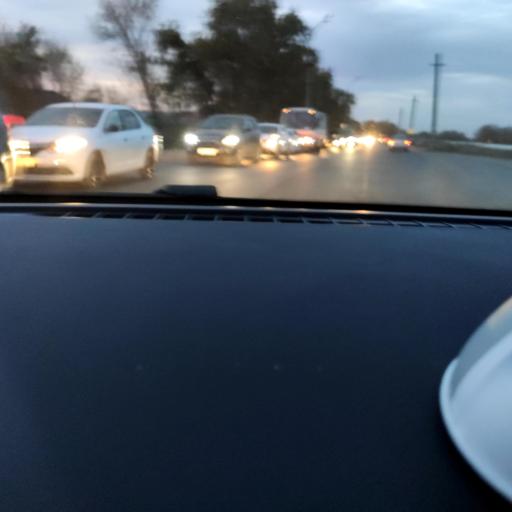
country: RU
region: Samara
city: Samara
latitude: 53.1397
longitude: 50.1013
